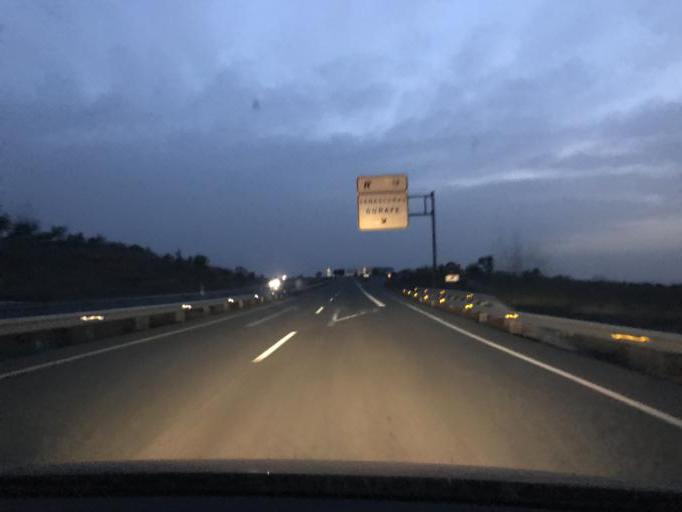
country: ES
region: Andalusia
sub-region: Provincia de Granada
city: Gor
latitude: 37.3979
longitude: -2.9837
